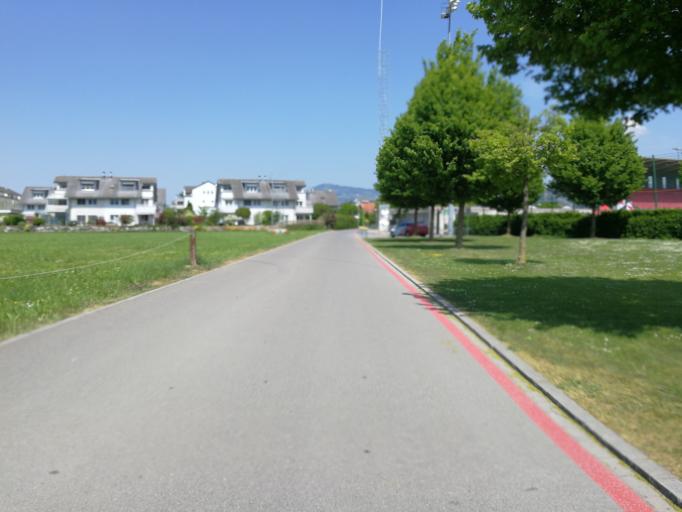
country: CH
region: Saint Gallen
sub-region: Wahlkreis See-Gaster
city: Jona
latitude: 47.2205
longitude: 8.8403
